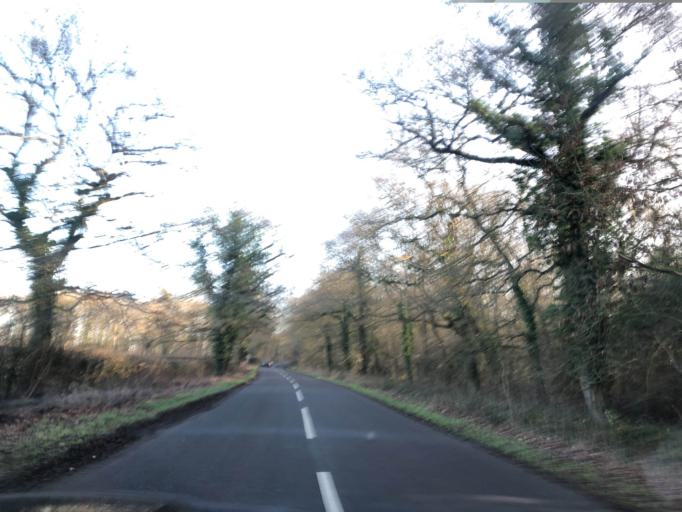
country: GB
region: England
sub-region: Warwickshire
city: Wellesbourne Mountford
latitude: 52.1896
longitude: -1.5356
